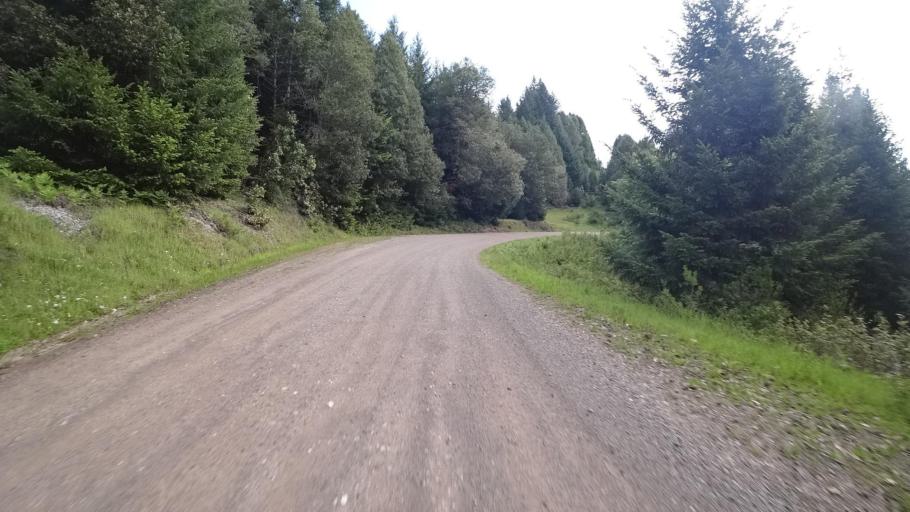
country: US
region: California
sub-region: Humboldt County
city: Redway
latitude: 40.2103
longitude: -123.6737
